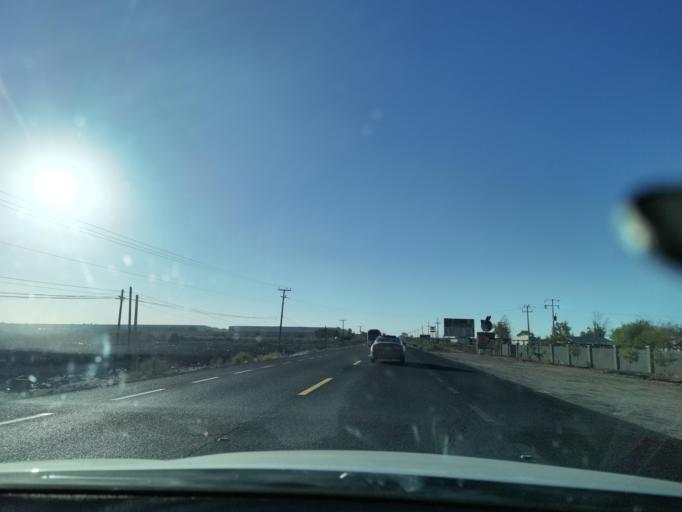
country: MX
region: Baja California
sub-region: Mexicali
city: Islas Agrarias Grupo A
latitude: 32.6379
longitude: -115.2883
